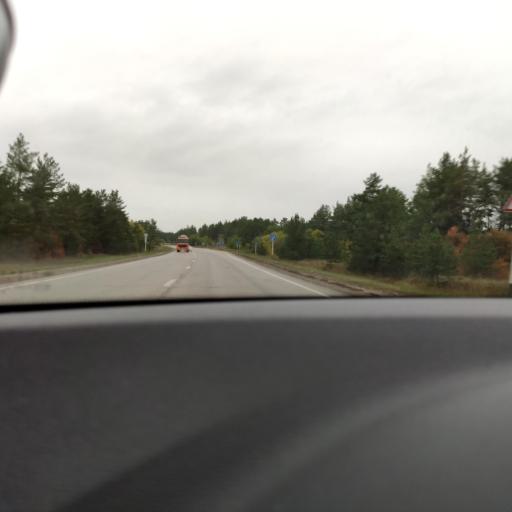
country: RU
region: Samara
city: Mirnyy
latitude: 53.5359
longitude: 50.3019
